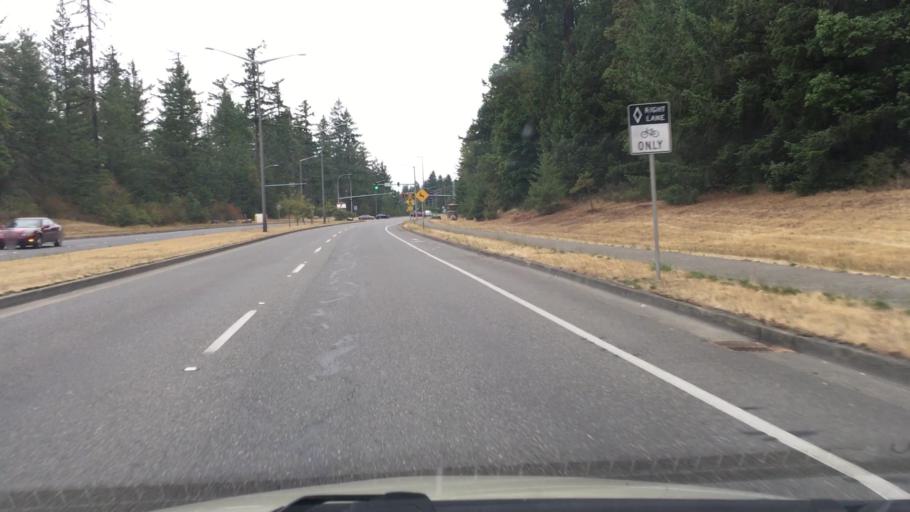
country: US
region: Washington
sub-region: Pierce County
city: Fort Lewis
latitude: 47.1083
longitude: -122.5929
